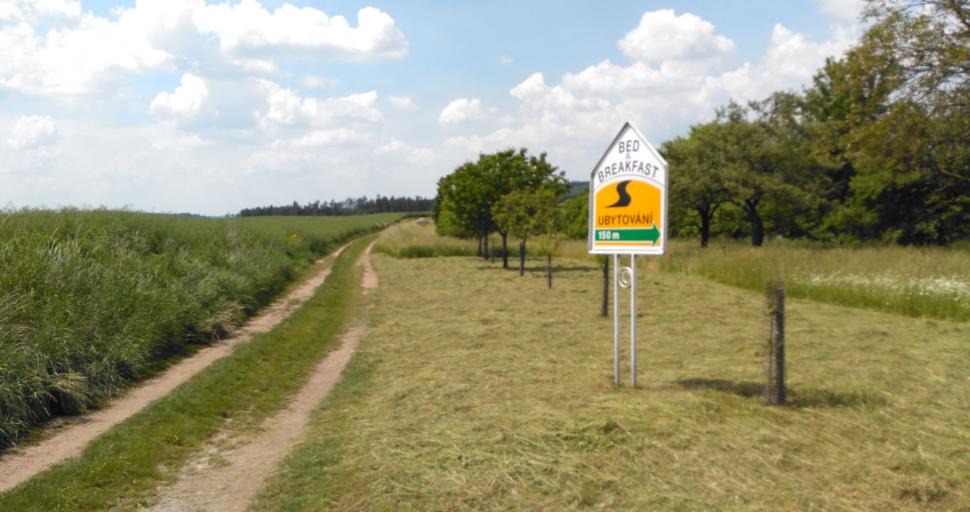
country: CZ
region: South Moravian
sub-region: Okres Blansko
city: Jedovnice
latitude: 49.3652
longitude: 16.7428
